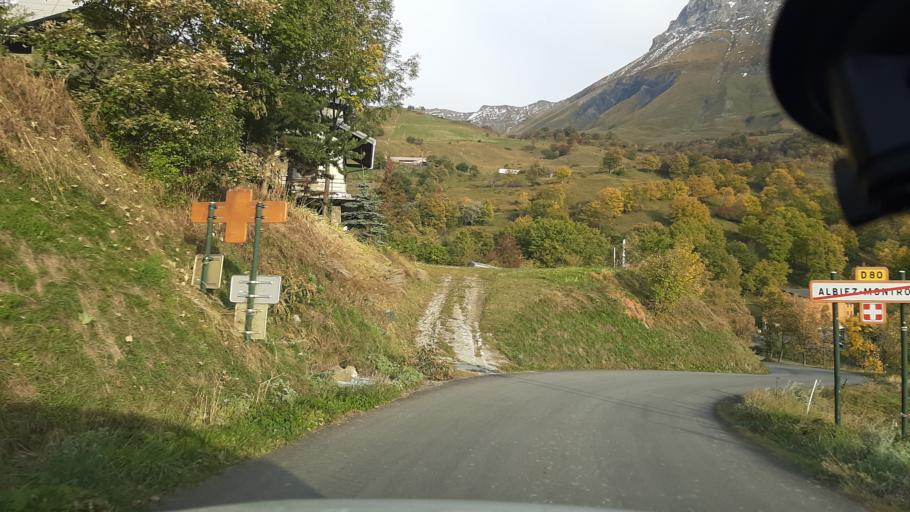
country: FR
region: Rhone-Alpes
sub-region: Departement de la Savoie
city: Villargondran
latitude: 45.2061
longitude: 6.3353
